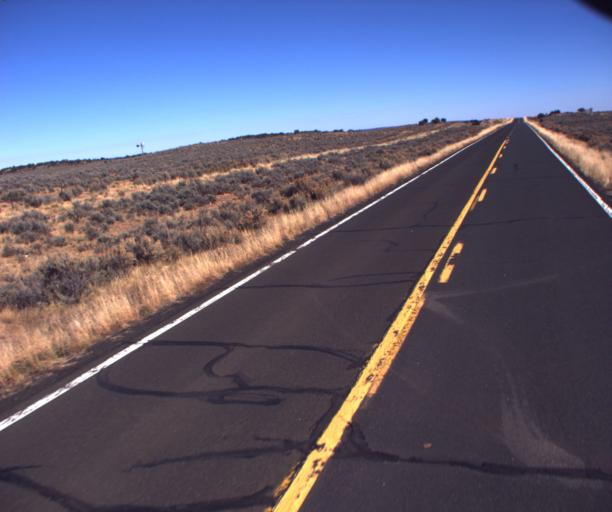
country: US
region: Arizona
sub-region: Navajo County
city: First Mesa
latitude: 35.7514
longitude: -110.0387
